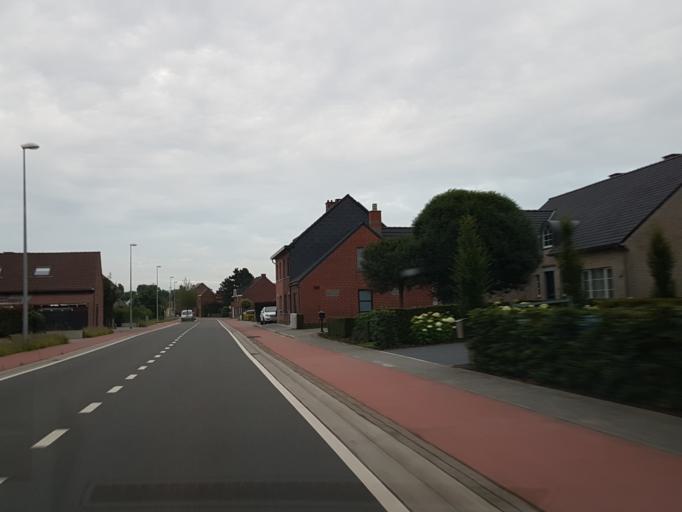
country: BE
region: Flanders
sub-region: Provincie Vlaams-Brabant
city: Zemst
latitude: 51.0079
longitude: 4.4169
